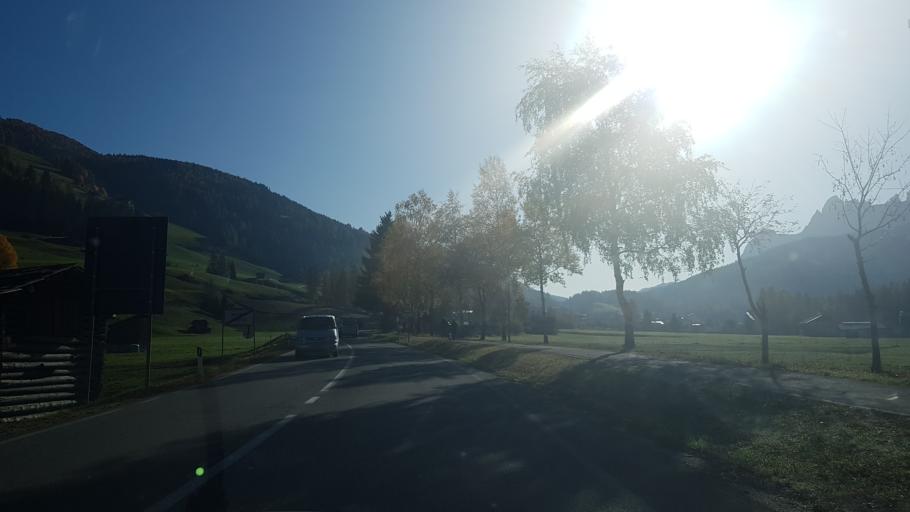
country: IT
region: Trentino-Alto Adige
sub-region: Bolzano
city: Sesto
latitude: 46.6963
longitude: 12.3572
